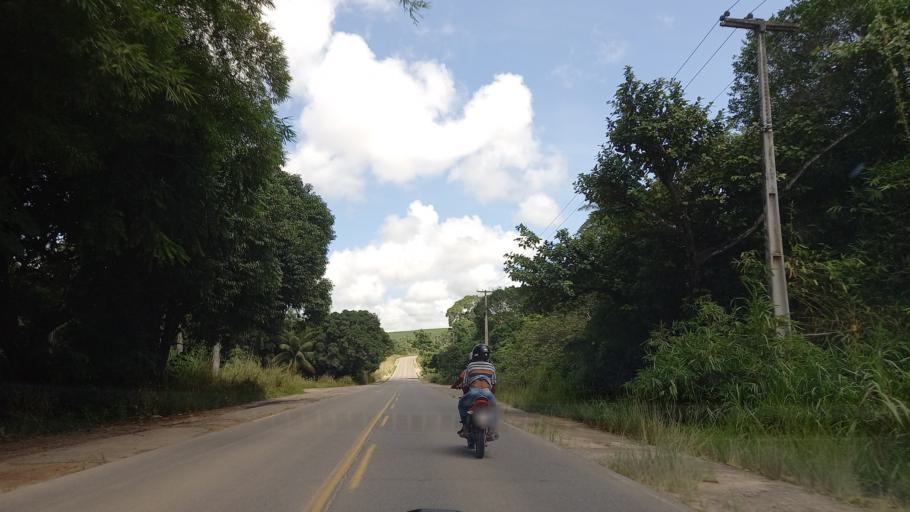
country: BR
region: Pernambuco
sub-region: Sirinhaem
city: Sirinhaem
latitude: -8.6143
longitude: -35.1198
